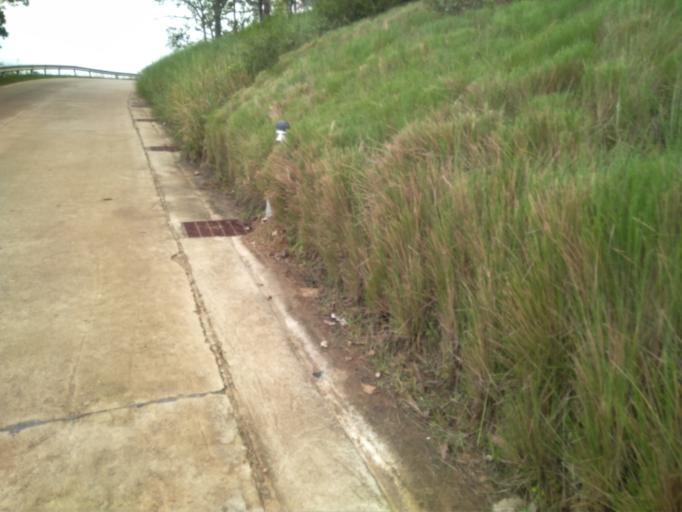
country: TH
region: Phangnga
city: Ko Yao
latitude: 8.1081
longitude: 98.6227
